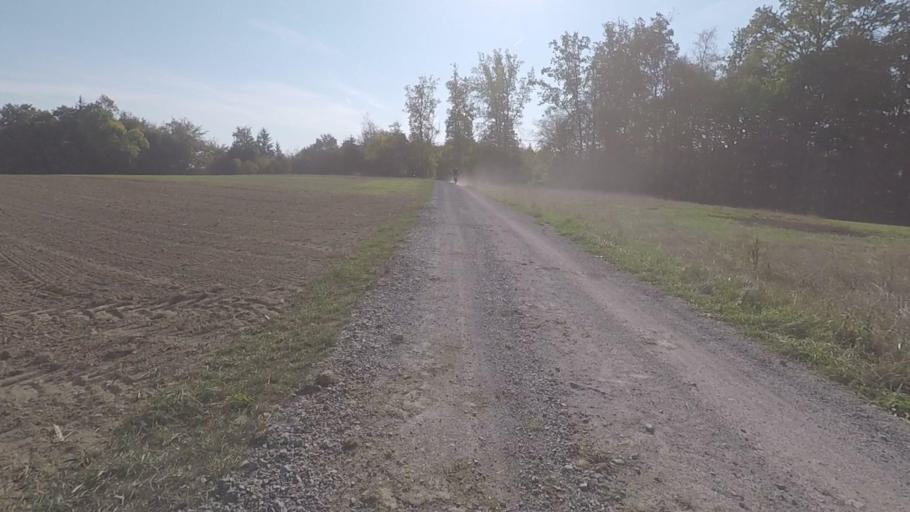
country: DE
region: Baden-Wuerttemberg
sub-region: Regierungsbezirk Stuttgart
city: Spiegelberg
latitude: 49.0420
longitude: 9.4785
